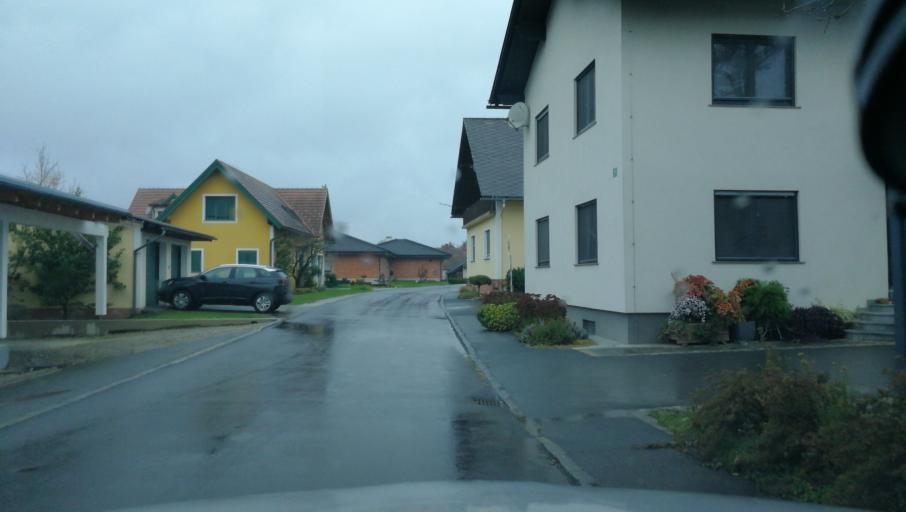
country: AT
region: Styria
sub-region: Politischer Bezirk Leibnitz
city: Strass in Steiermark
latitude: 46.7384
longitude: 15.6447
